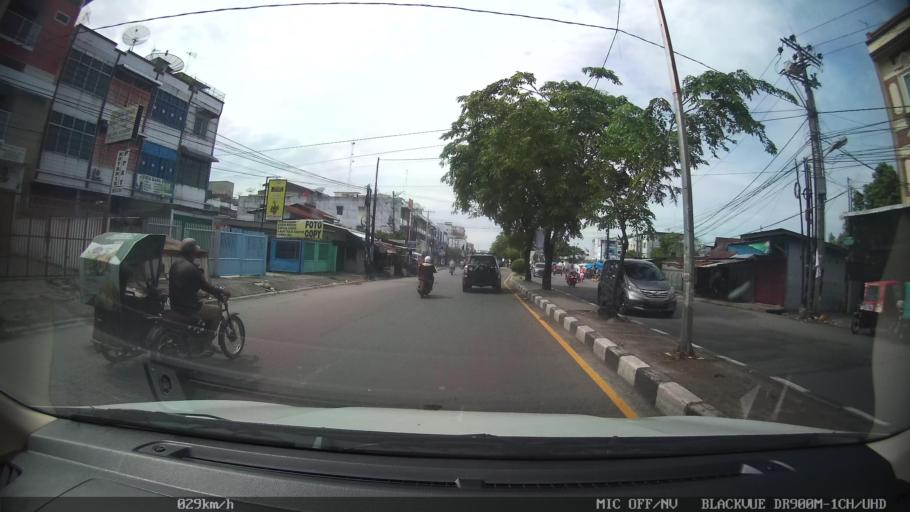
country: ID
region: North Sumatra
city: Medan
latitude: 3.5995
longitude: 98.7065
